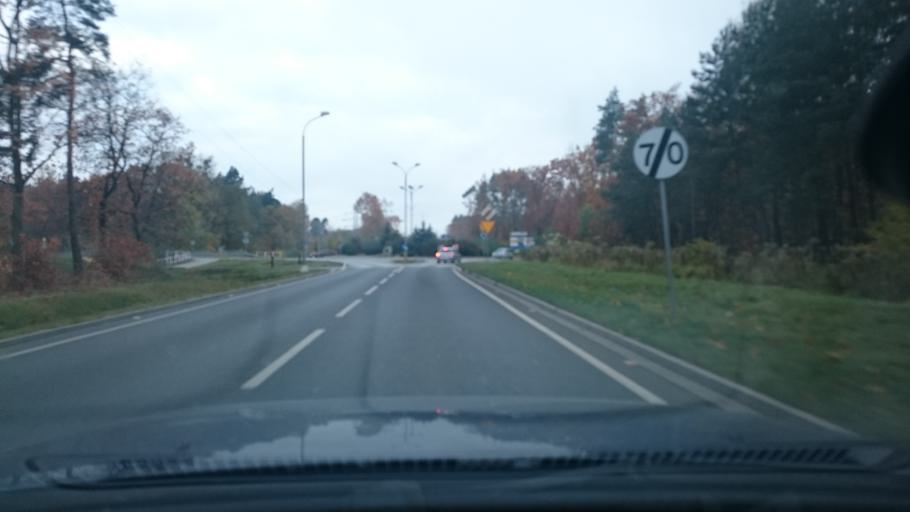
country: PL
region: Silesian Voivodeship
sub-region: Rybnik
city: Rybnik
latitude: 50.1142
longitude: 18.5551
